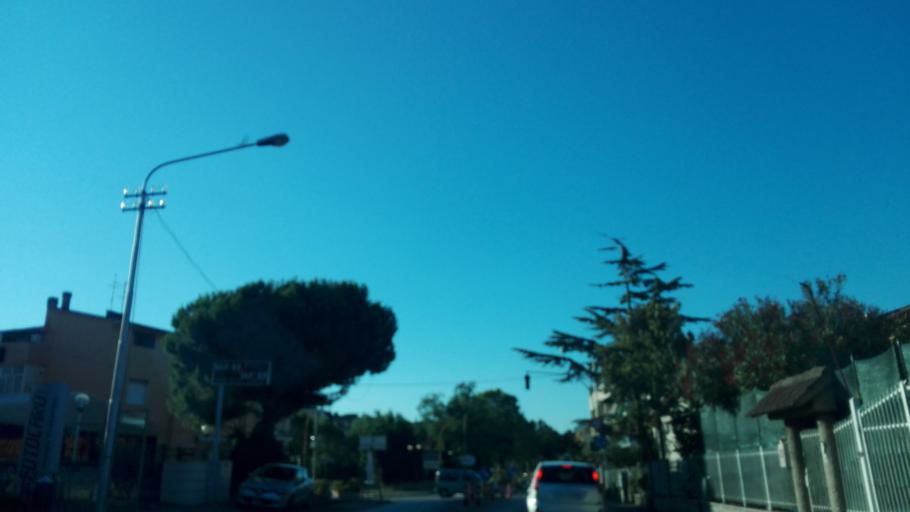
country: IT
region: Abruzzo
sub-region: Provincia di Pescara
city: Villa Raspa
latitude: 42.4934
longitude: 14.1747
